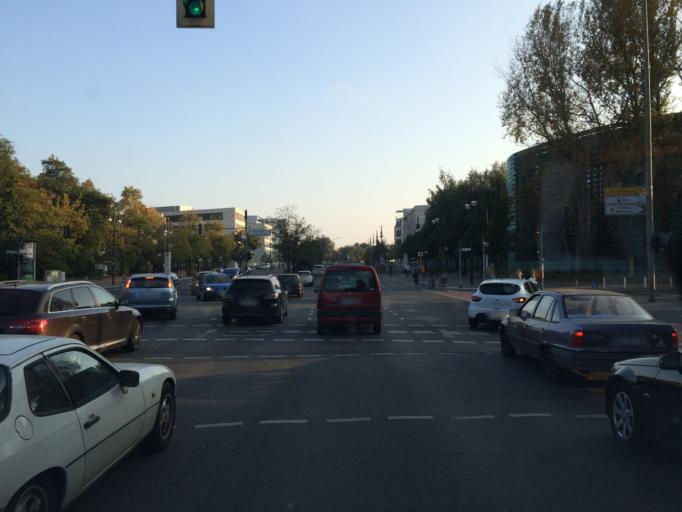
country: DE
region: Berlin
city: Hansaviertel
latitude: 52.5099
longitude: 13.3512
